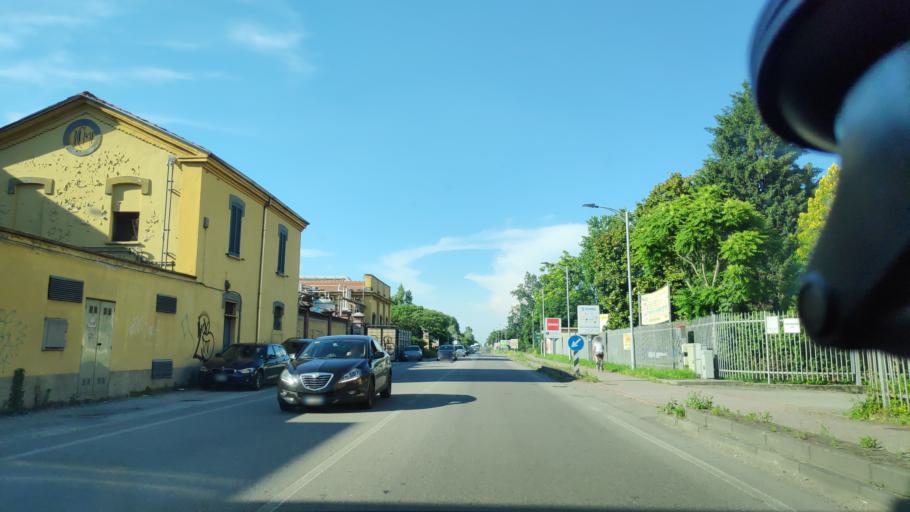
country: IT
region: Lombardy
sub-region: Citta metropolitana di Milano
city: Rozzano
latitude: 45.3815
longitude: 9.1439
